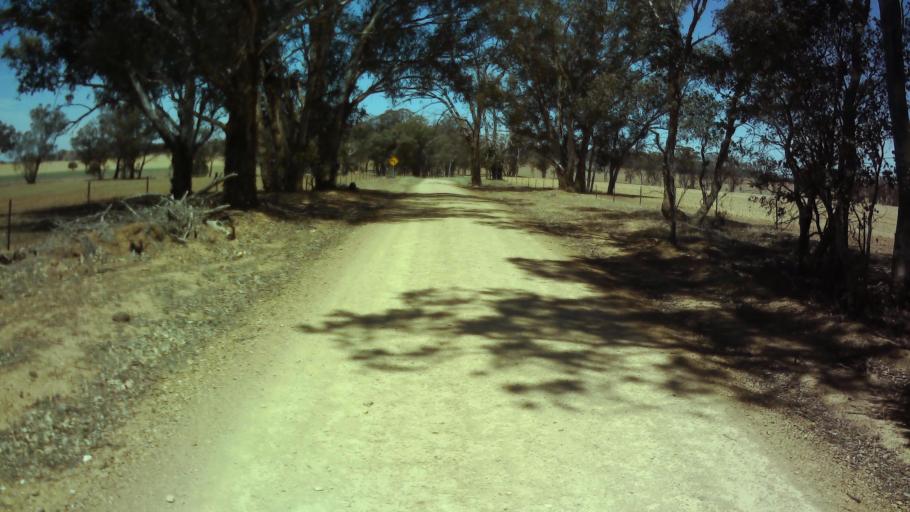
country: AU
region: New South Wales
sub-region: Weddin
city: Grenfell
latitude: -33.9215
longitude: 148.2100
